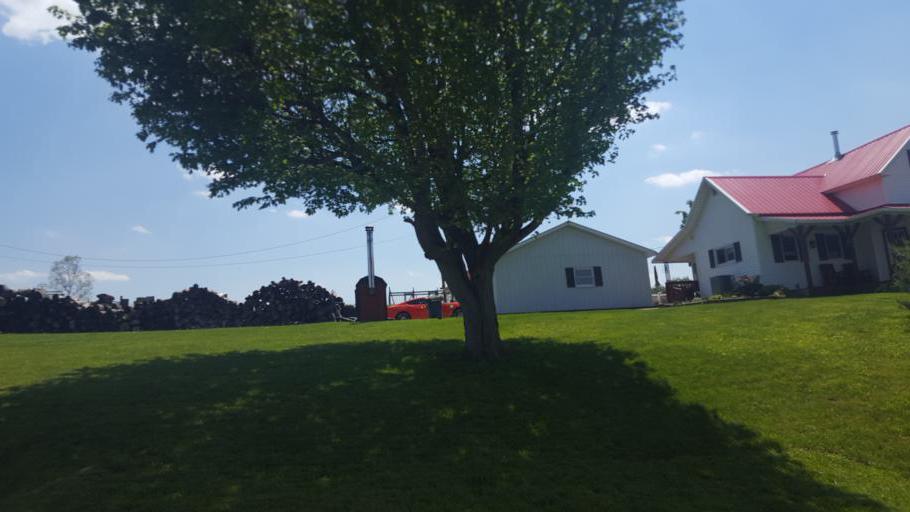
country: US
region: Ohio
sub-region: Knox County
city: Oak Hill
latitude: 40.2853
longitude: -82.2707
